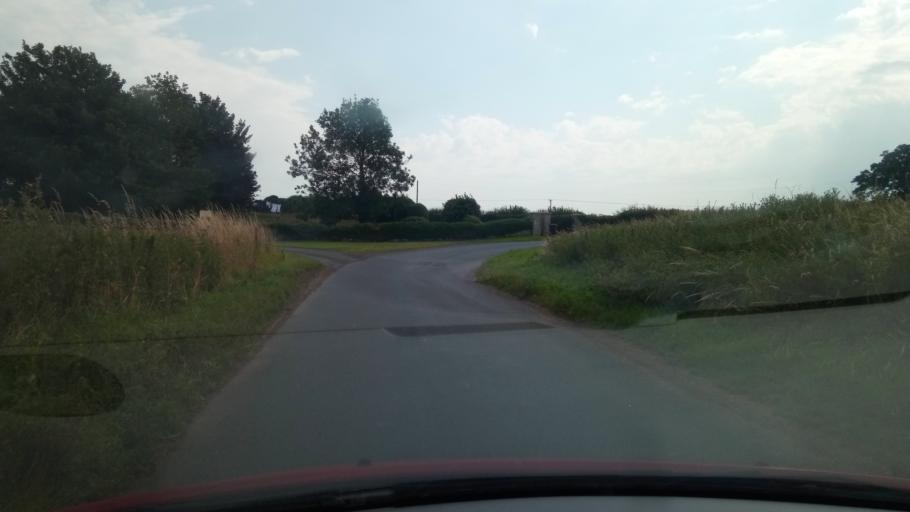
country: GB
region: Scotland
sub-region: The Scottish Borders
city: Kelso
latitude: 55.5895
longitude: -2.4700
